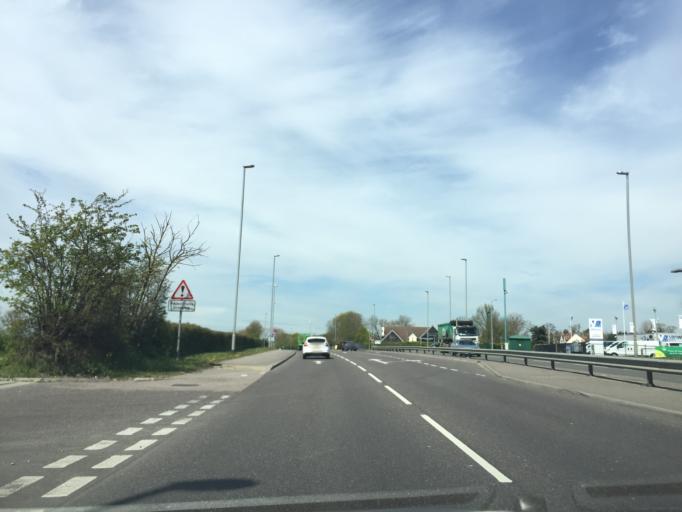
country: GB
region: England
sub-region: Essex
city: Harlow
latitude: 51.7494
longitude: 0.1341
